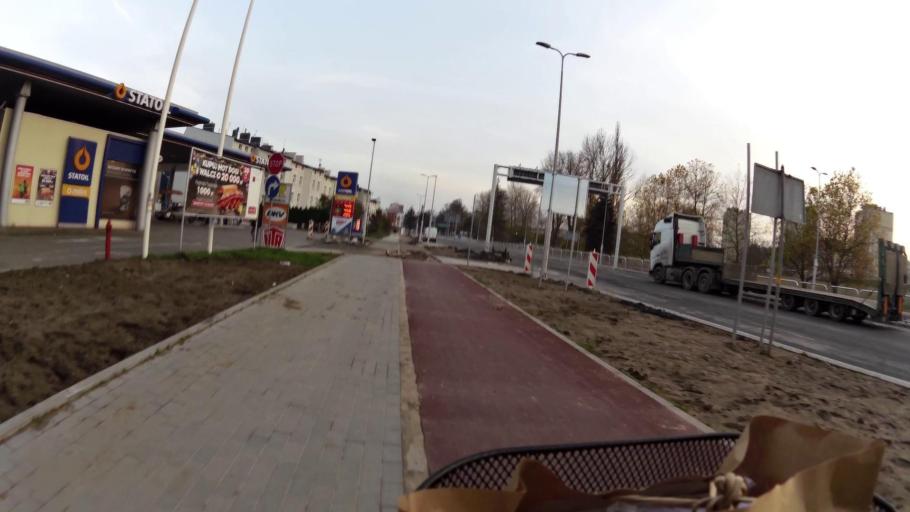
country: PL
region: West Pomeranian Voivodeship
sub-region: Koszalin
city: Koszalin
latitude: 54.1882
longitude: 16.1738
